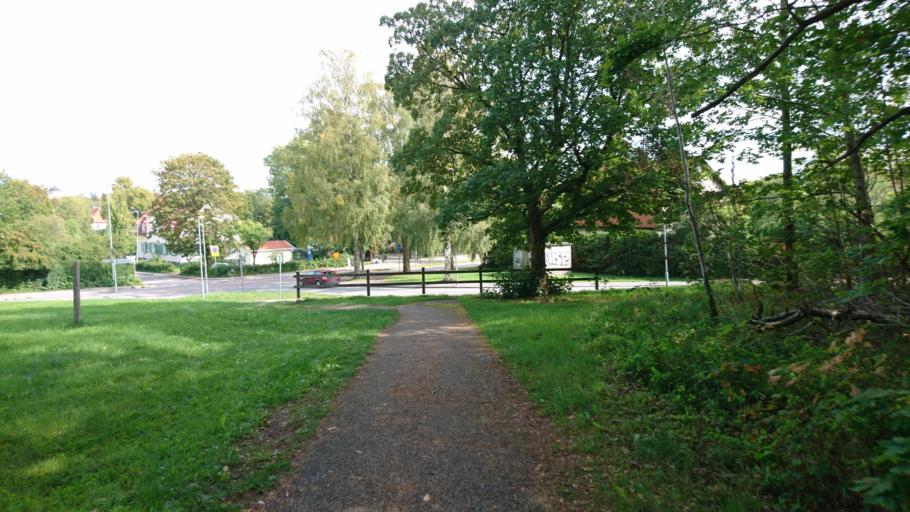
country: SE
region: Uppsala
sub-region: Uppsala Kommun
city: Uppsala
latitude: 59.8464
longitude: 17.6236
